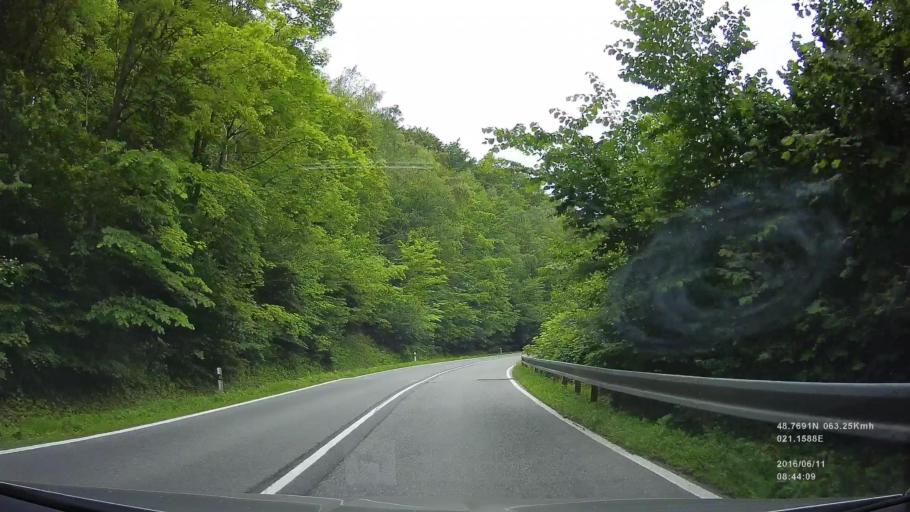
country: SK
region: Kosicky
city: Kosice
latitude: 48.7575
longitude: 21.1896
